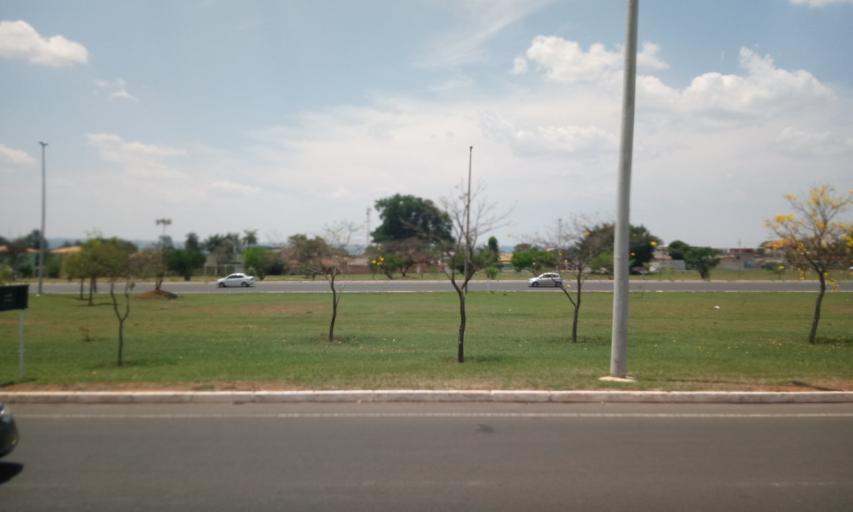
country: BR
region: Federal District
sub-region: Brasilia
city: Brasilia
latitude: -15.7951
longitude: -47.8562
